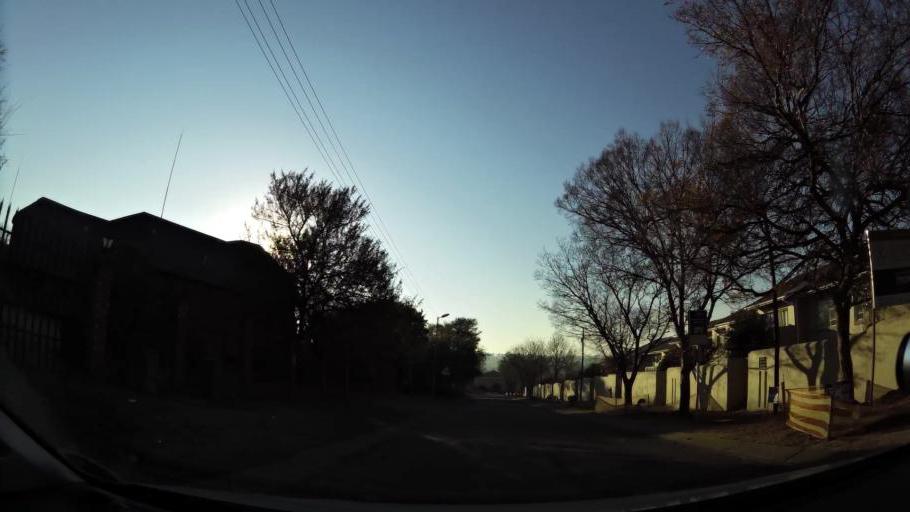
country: ZA
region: Gauteng
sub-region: City of Johannesburg Metropolitan Municipality
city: Midrand
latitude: -26.0474
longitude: 28.1056
